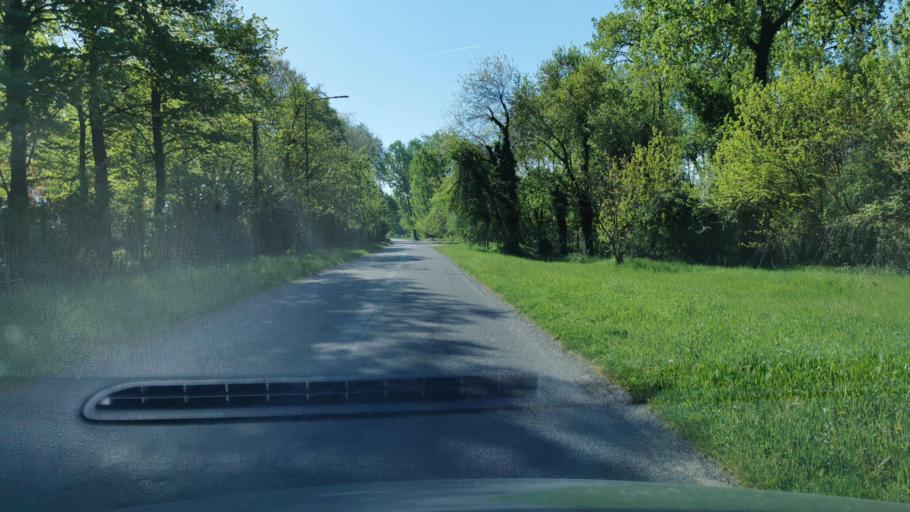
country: IT
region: Lombardy
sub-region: Provincia di Cremona
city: Cremona
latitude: 45.1208
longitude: 10.0078
